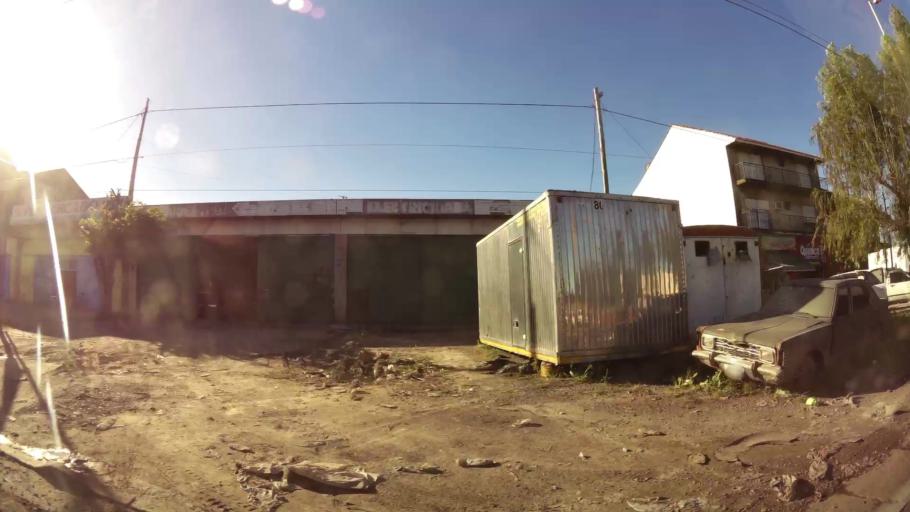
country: AR
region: Buenos Aires
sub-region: Partido de Quilmes
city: Quilmes
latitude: -34.7432
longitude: -58.3256
